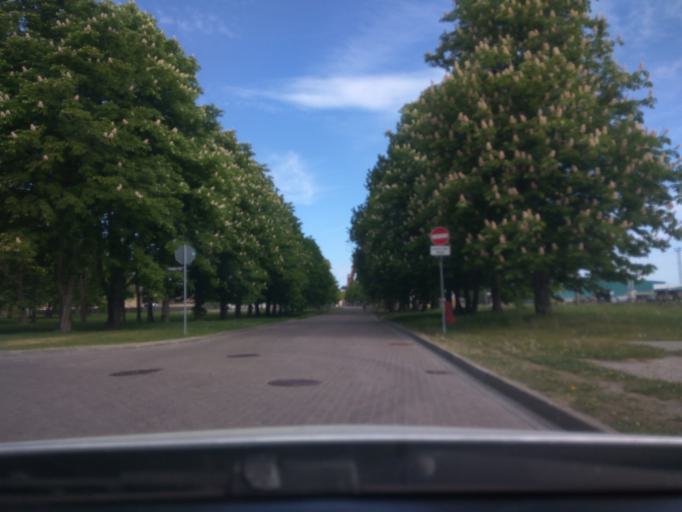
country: LV
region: Ventspils
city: Ventspils
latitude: 57.3953
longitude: 21.5730
